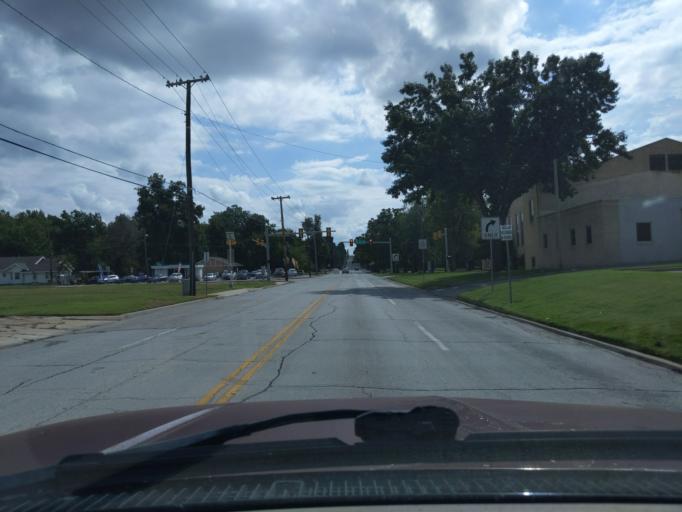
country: US
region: Oklahoma
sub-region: Tulsa County
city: Tulsa
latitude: 36.1052
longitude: -96.0116
